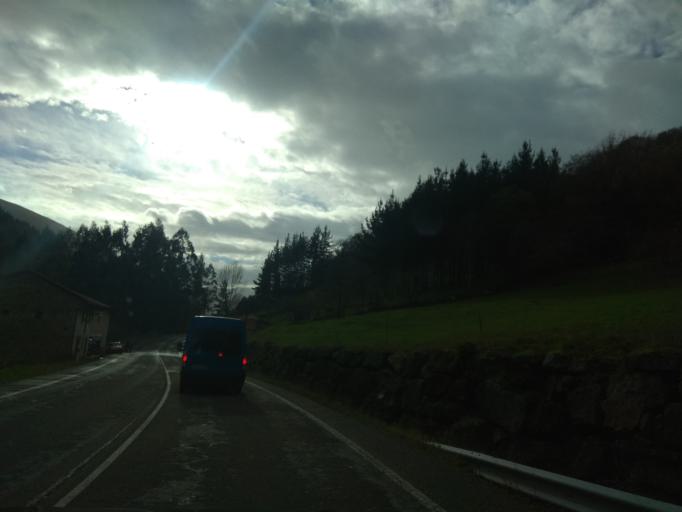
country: ES
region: Cantabria
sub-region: Provincia de Cantabria
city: San Pedro del Romeral
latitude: 43.1524
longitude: -3.8976
